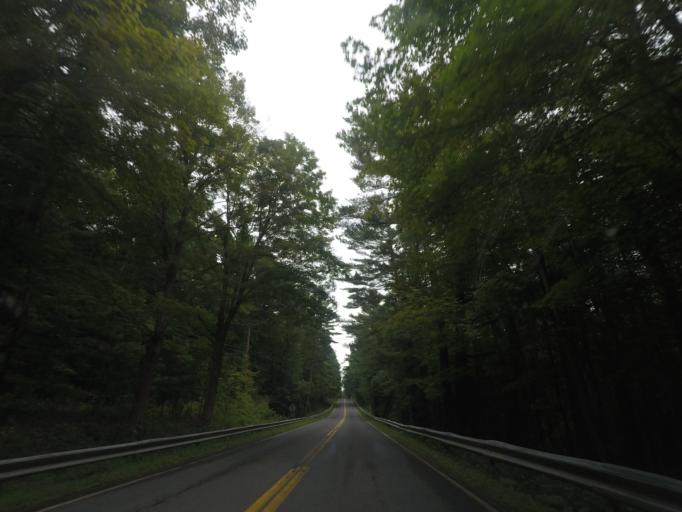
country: US
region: New York
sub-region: Columbia County
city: Chatham
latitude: 42.4283
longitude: -73.5496
